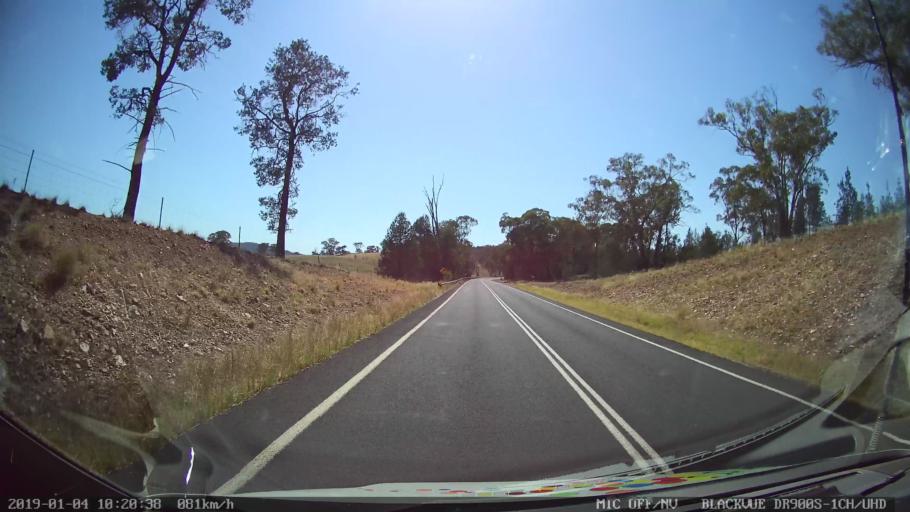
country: AU
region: New South Wales
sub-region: Cabonne
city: Canowindra
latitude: -33.3719
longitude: 148.4986
